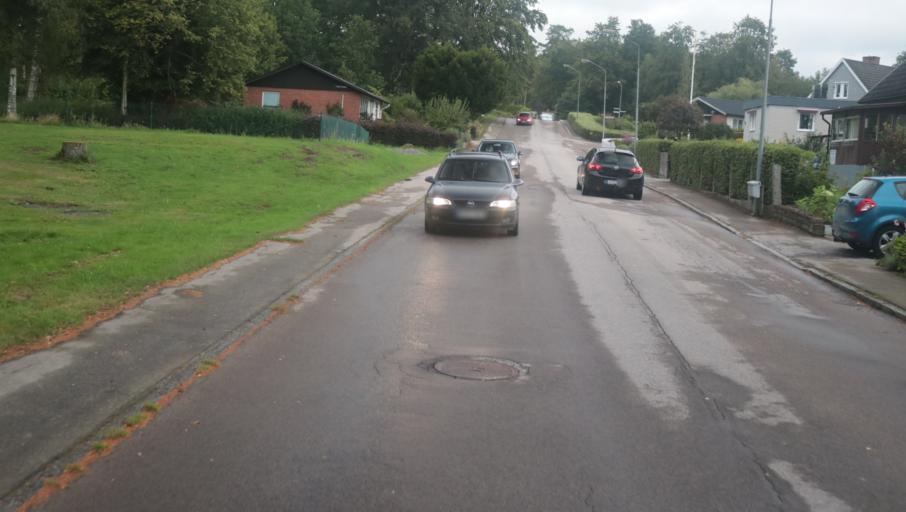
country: SE
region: Blekinge
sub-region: Karlshamns Kommun
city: Svangsta
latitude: 56.2583
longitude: 14.7785
